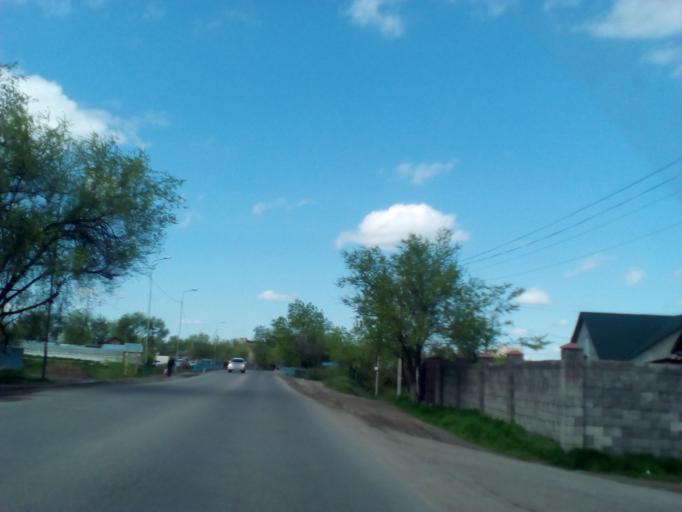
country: KZ
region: Almaty Oblysy
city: Burunday
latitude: 43.2079
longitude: 76.6369
